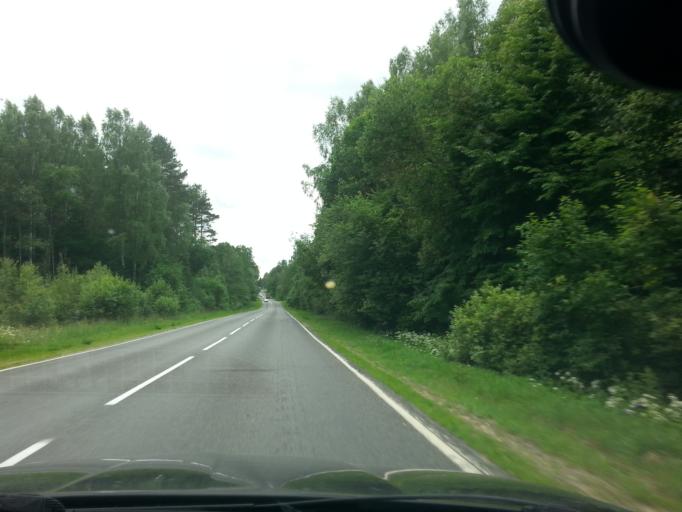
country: BY
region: Minsk
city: Svir
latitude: 54.8734
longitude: 26.3543
